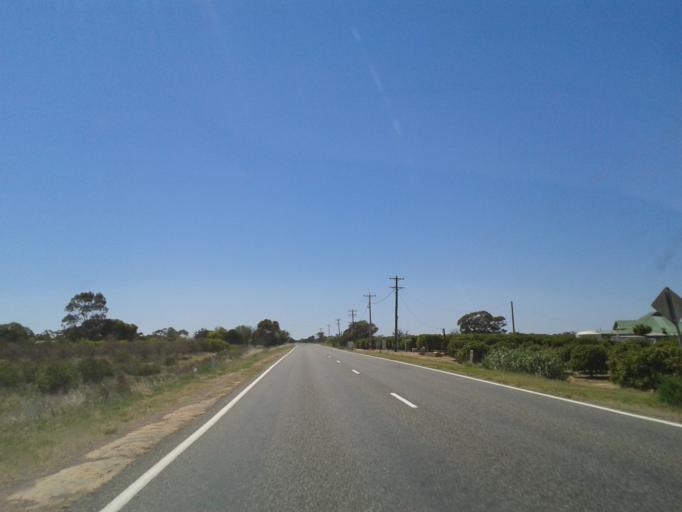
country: AU
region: New South Wales
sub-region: Wentworth
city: Dareton
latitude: -34.1057
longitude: 141.9923
